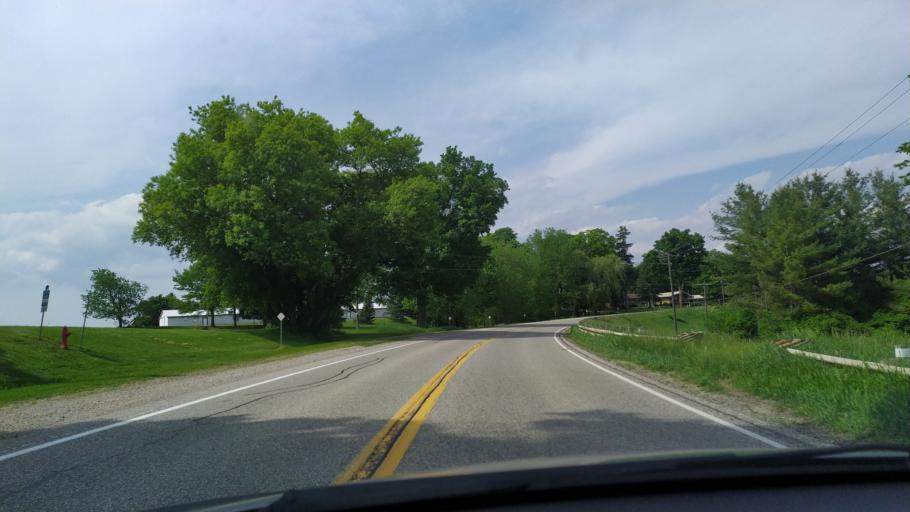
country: CA
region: Ontario
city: Dorchester
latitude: 43.0730
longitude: -81.0066
